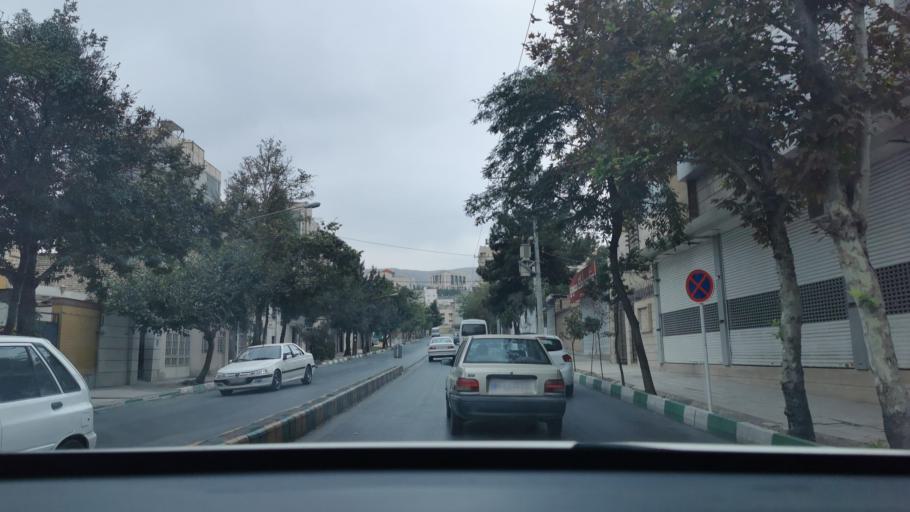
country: IR
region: Razavi Khorasan
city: Mashhad
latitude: 36.3078
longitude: 59.5019
